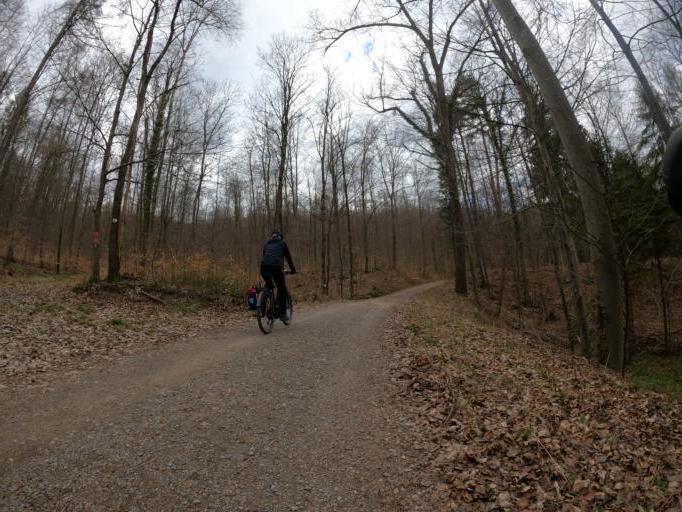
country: DE
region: Baden-Wuerttemberg
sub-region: Tuebingen Region
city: Mossingen
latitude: 48.3810
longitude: 9.0524
